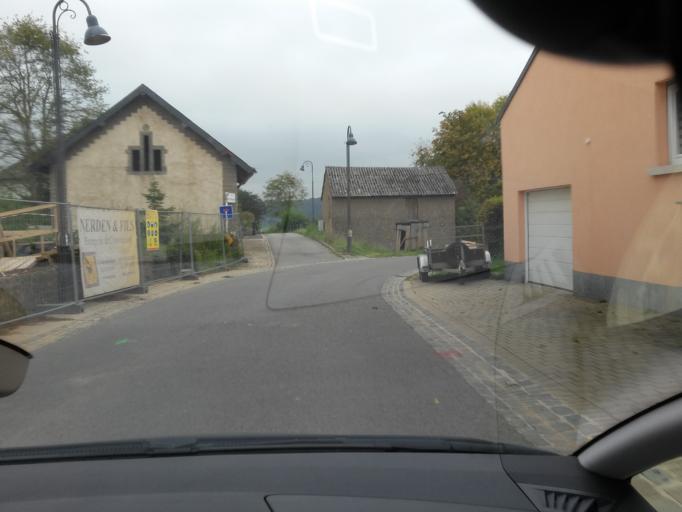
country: LU
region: Luxembourg
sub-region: Canton de Capellen
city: Hobscheid
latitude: 49.7232
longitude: 5.9283
